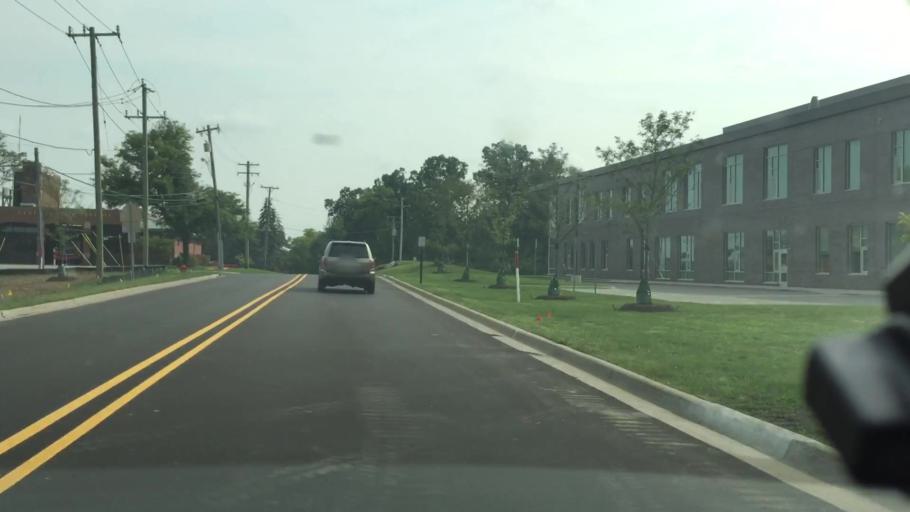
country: US
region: Michigan
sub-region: Oakland County
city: Bloomfield Hills
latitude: 42.5788
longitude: -83.2847
